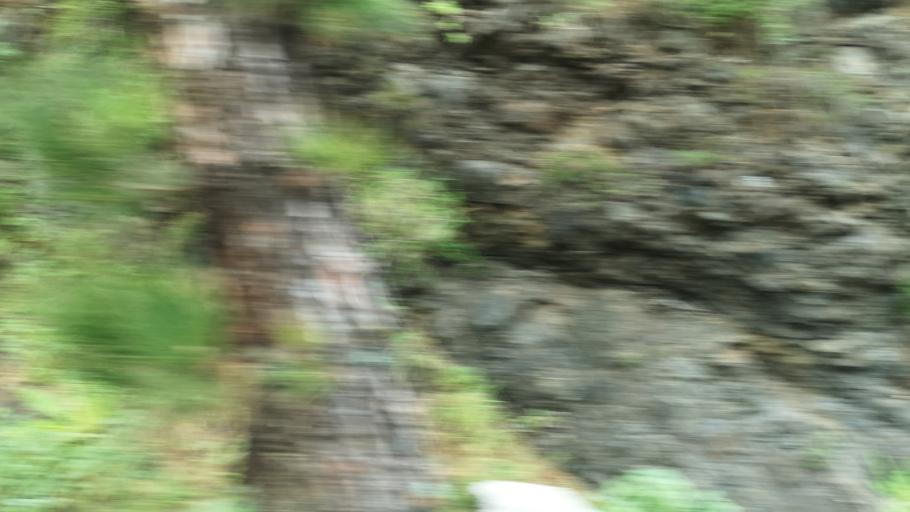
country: ES
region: Canary Islands
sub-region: Provincia de Santa Cruz de Tenerife
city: Hermigua
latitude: 28.1359
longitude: -17.2011
